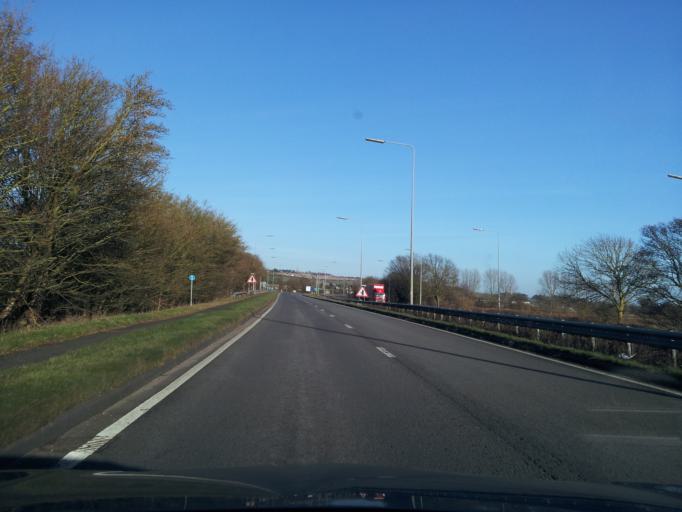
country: GB
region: England
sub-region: Northamptonshire
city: Bugbrooke
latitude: 52.2342
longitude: -0.9887
